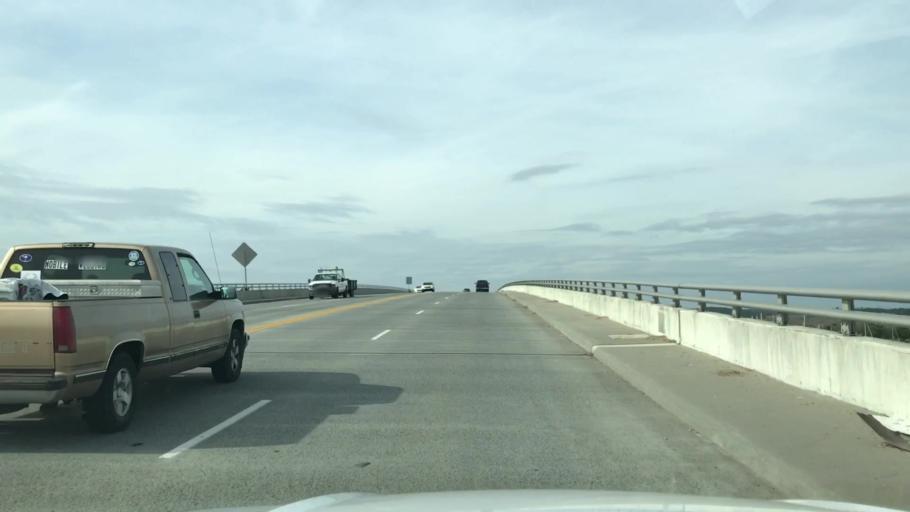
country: US
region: South Carolina
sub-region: Charleston County
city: Charleston
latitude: 32.7530
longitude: -80.0080
